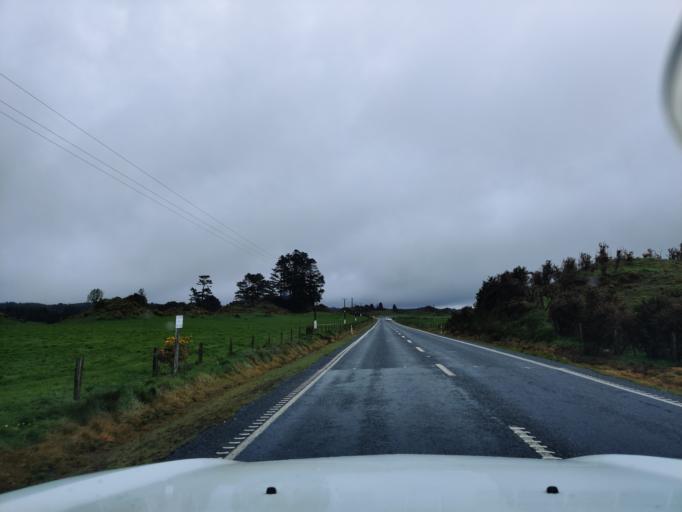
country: NZ
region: Bay of Plenty
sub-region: Rotorua District
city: Rotorua
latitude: -38.0474
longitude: 176.0720
